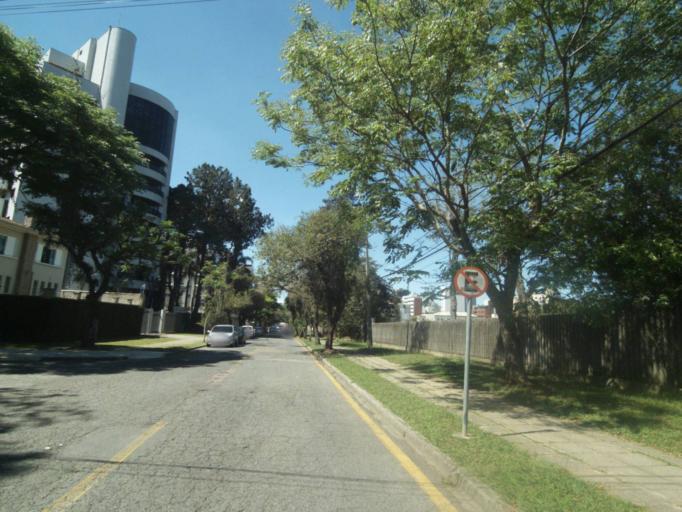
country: BR
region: Parana
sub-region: Curitiba
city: Curitiba
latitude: -25.4098
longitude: -49.2506
